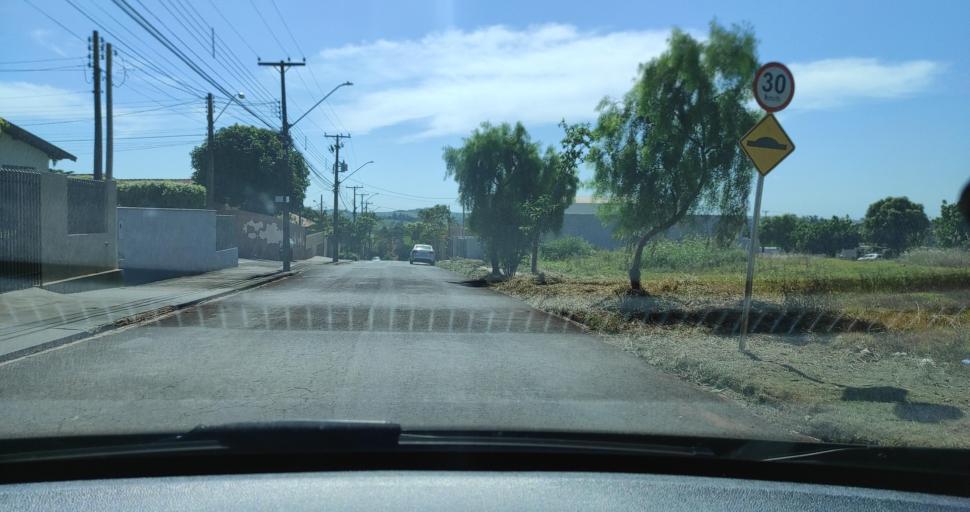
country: BR
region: Parana
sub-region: Ibipora
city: Ibipora
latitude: -23.2585
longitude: -51.0585
